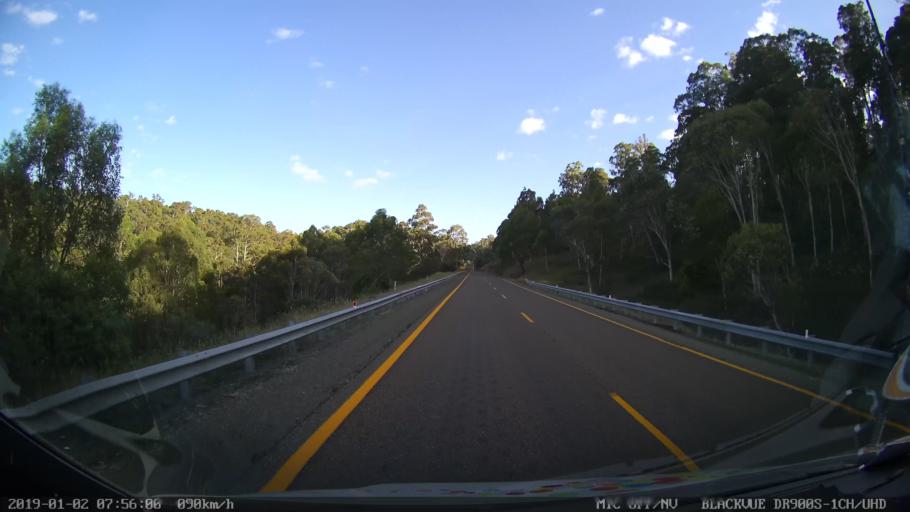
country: AU
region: New South Wales
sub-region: Tumut Shire
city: Tumut
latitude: -35.6761
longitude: 148.4861
